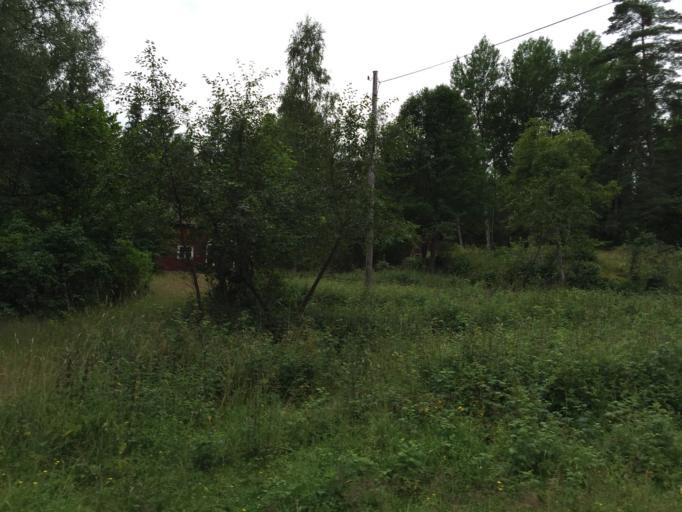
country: SE
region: Soedermanland
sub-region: Vingakers Kommun
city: Vingaker
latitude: 59.0086
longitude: 15.7239
